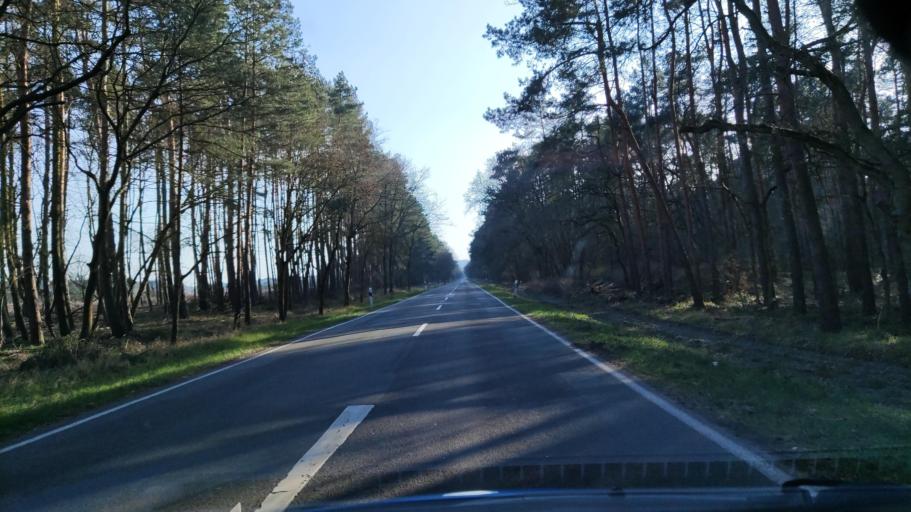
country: DE
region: Saxony-Anhalt
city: Seehausen
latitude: 52.8713
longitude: 11.7403
